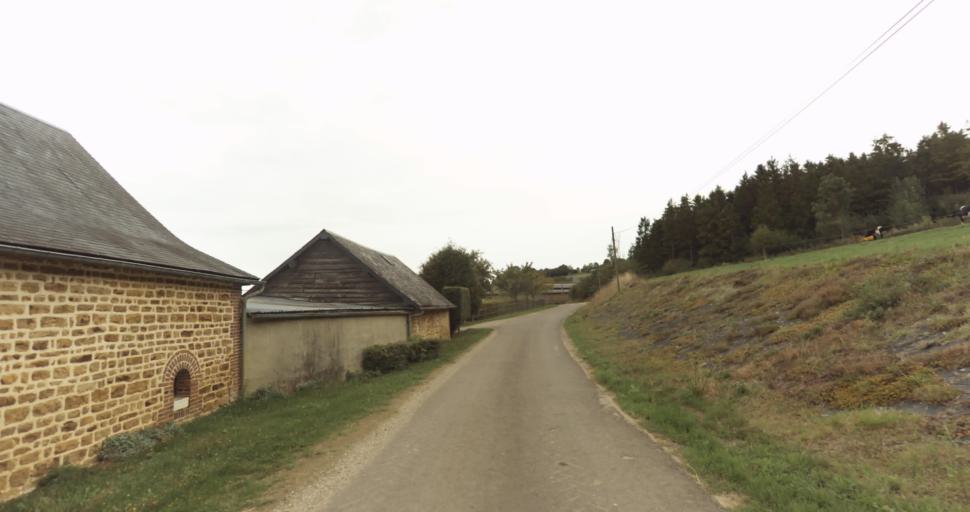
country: FR
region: Lower Normandy
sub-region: Departement de l'Orne
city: Gace
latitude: 48.7578
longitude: 0.3363
